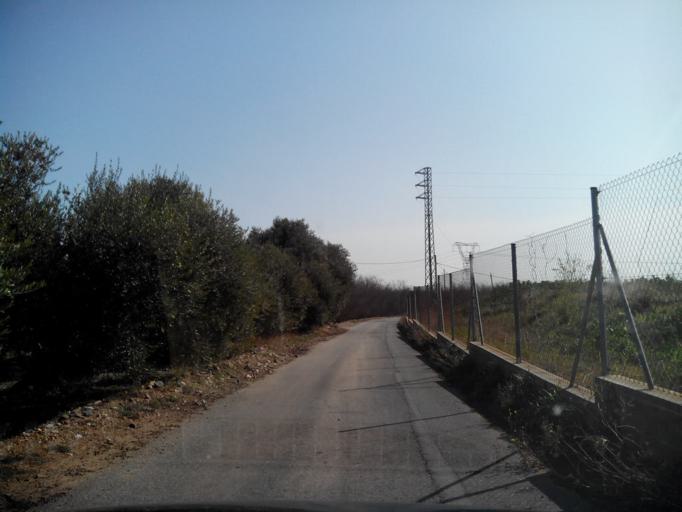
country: ES
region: Catalonia
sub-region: Provincia de Tarragona
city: La Selva
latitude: 41.2131
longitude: 1.1651
